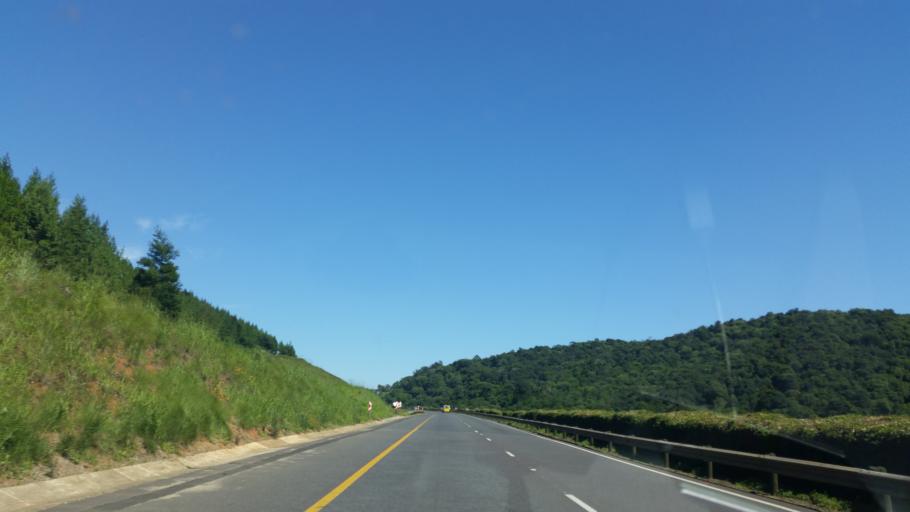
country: ZA
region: KwaZulu-Natal
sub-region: uMgungundlovu District Municipality
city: Mooirivier
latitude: -29.3408
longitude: 30.0775
